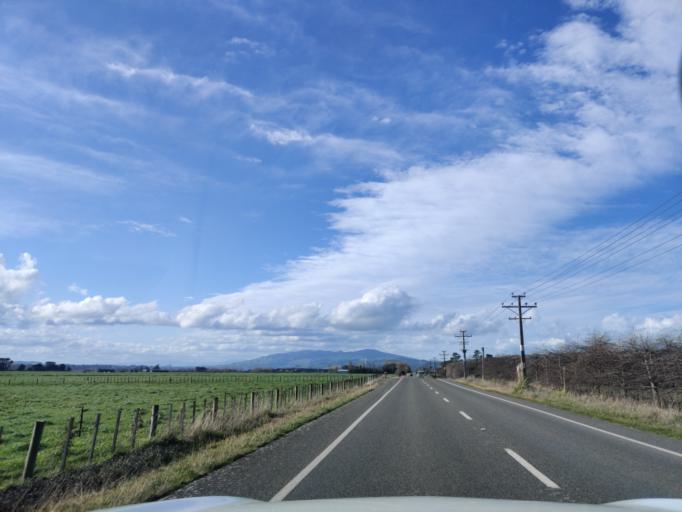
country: NZ
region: Manawatu-Wanganui
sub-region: Palmerston North City
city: Palmerston North
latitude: -40.3531
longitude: 175.6931
